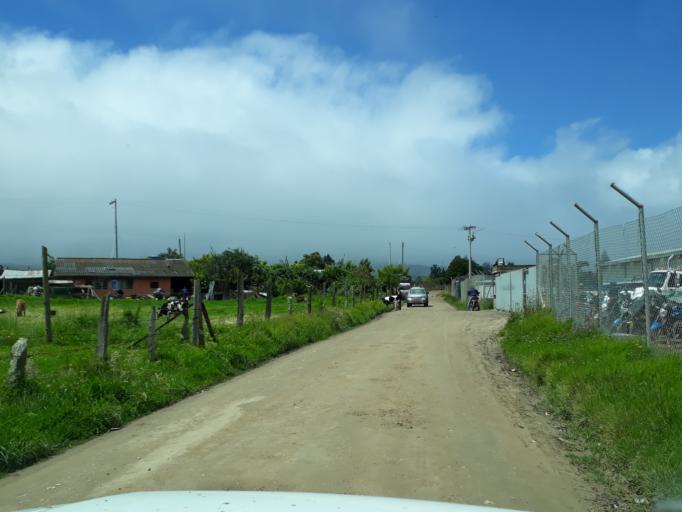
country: CO
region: Cundinamarca
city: Guasca
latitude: 4.8820
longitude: -73.8828
